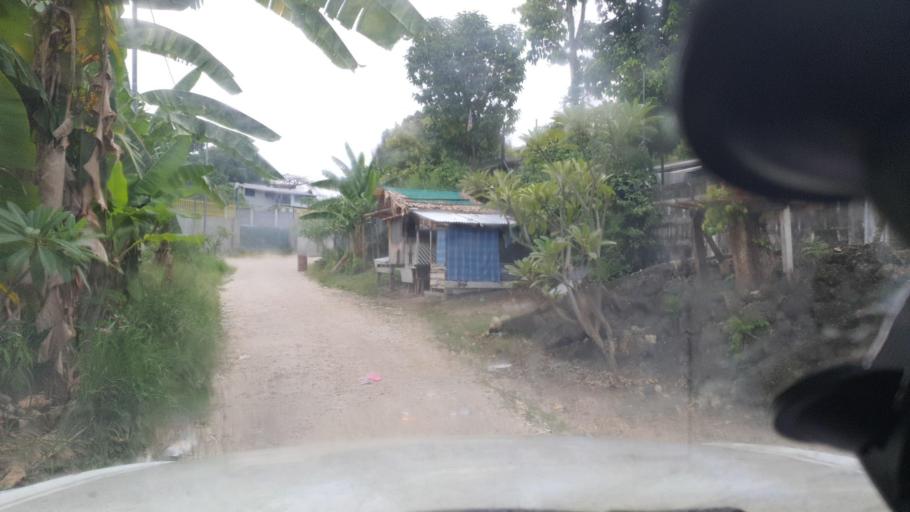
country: SB
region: Guadalcanal
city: Honiara
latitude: -9.4336
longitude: 159.9463
